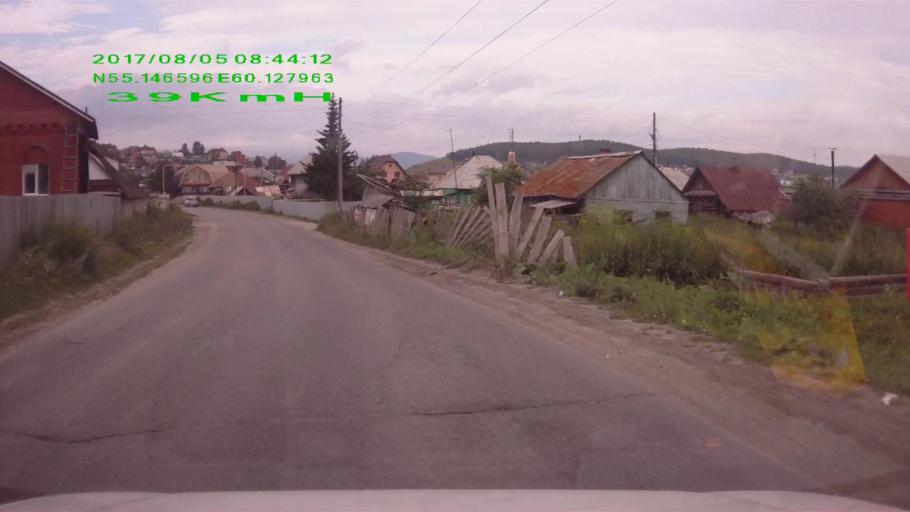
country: RU
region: Chelyabinsk
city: Turgoyak
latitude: 55.1466
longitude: 60.1273
